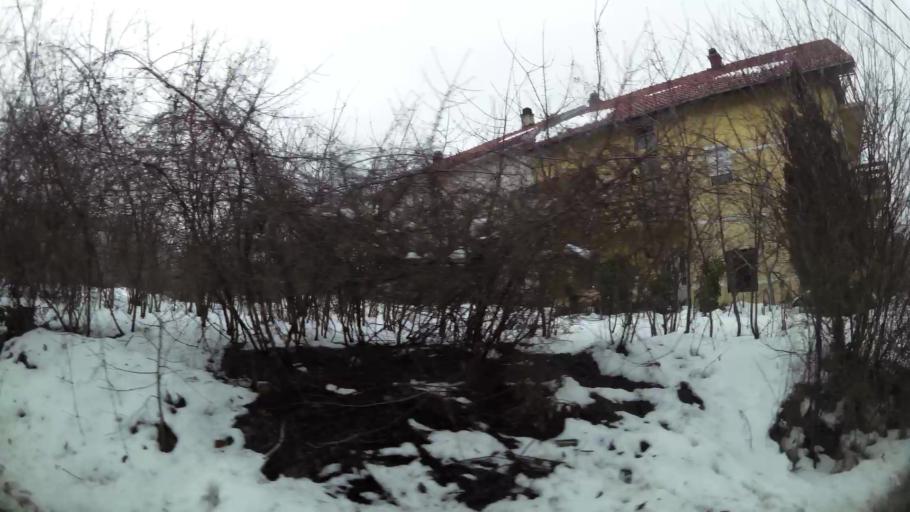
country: RS
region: Central Serbia
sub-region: Belgrade
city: Zvezdara
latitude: 44.7647
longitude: 20.5198
